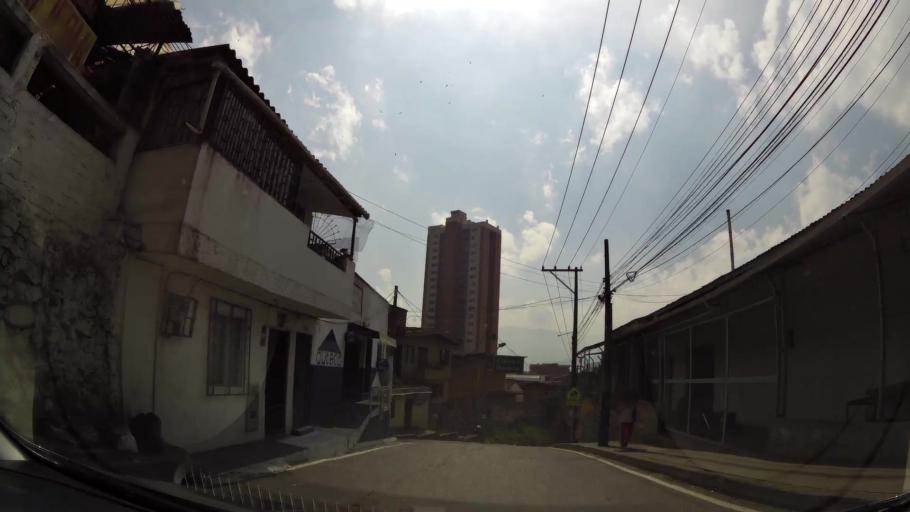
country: CO
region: Antioquia
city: La Estrella
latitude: 6.1755
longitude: -75.6360
